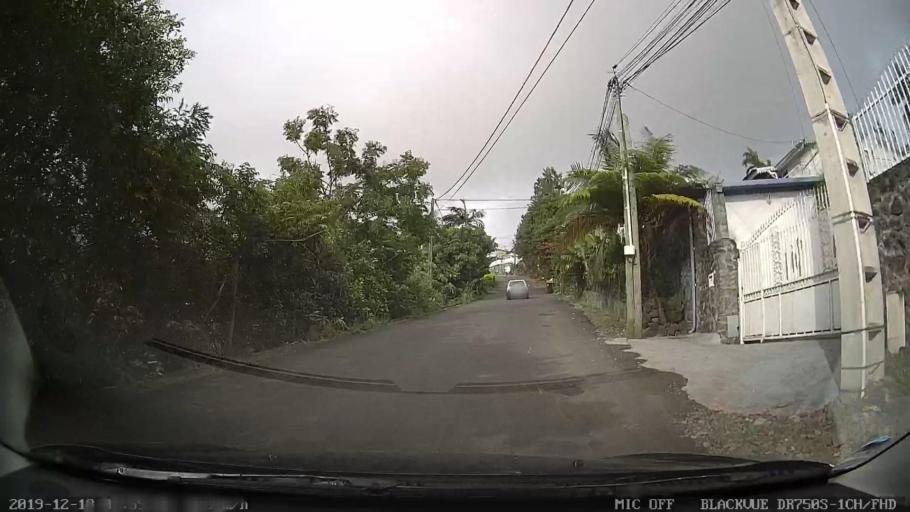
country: RE
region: Reunion
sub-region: Reunion
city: Le Tampon
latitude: -21.2552
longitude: 55.5164
